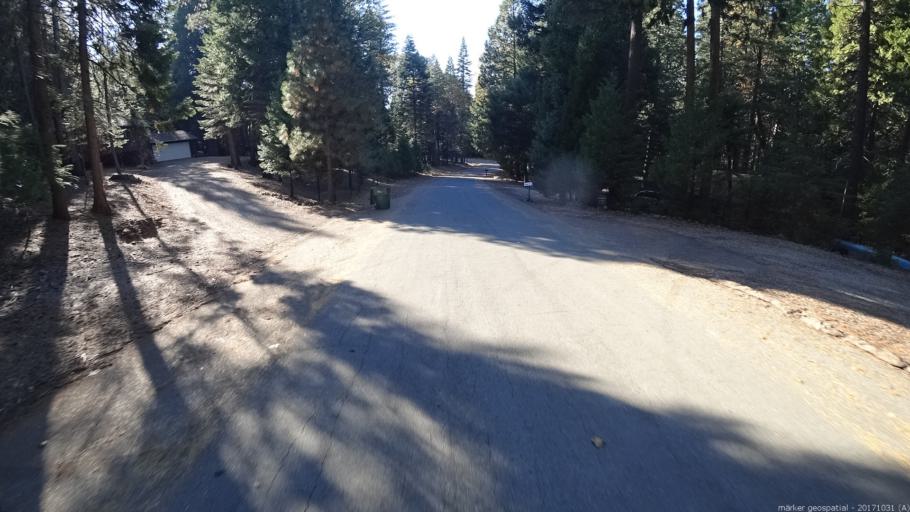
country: US
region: California
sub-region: Shasta County
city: Shingletown
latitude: 40.5017
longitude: -121.9007
